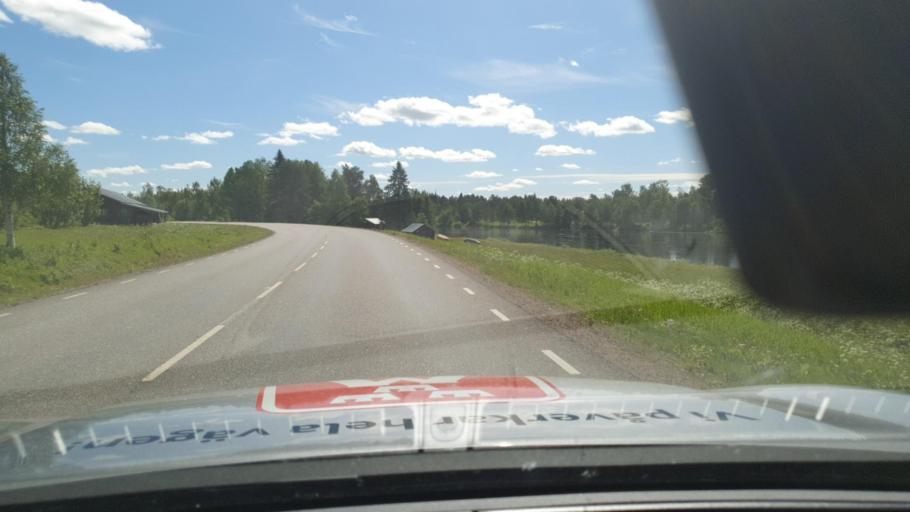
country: SE
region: Norrbotten
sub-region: Pajala Kommun
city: Pajala
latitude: 67.1629
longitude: 22.6239
